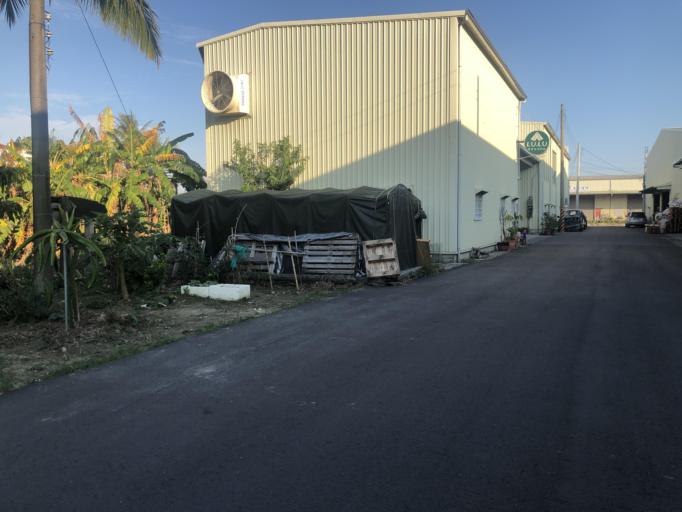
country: TW
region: Taiwan
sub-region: Tainan
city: Tainan
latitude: 23.0370
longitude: 120.1840
